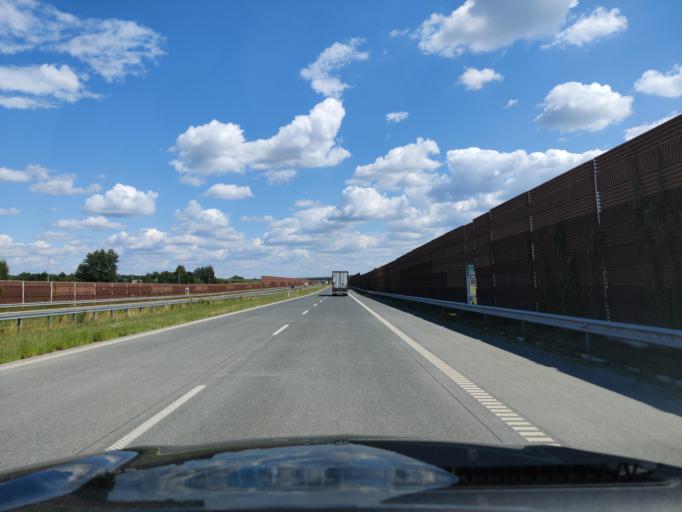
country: PL
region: Masovian Voivodeship
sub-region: Powiat minski
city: Halinow
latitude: 52.2150
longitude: 21.3914
